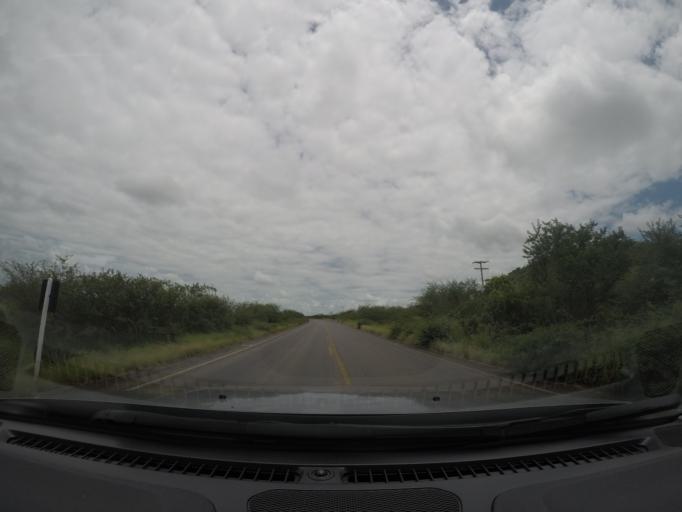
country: BR
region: Bahia
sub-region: Itaberaba
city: Itaberaba
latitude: -12.5010
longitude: -40.2462
